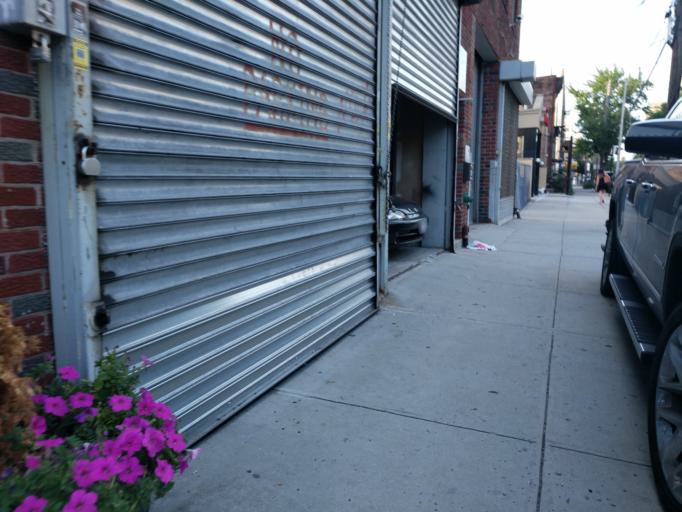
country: US
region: New York
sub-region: Queens County
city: Long Island City
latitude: 40.7549
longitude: -73.9367
